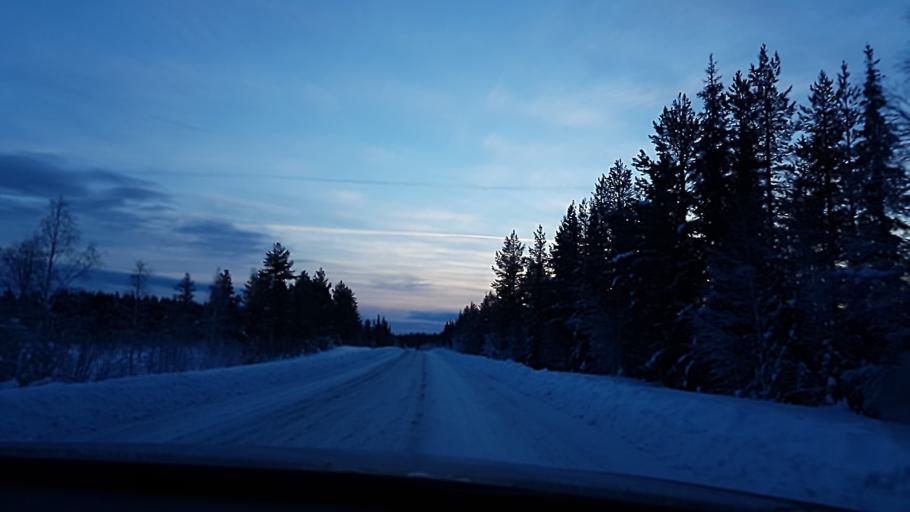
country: SE
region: Norrbotten
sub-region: Jokkmokks Kommun
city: Jokkmokk
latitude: 66.1190
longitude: 20.0338
